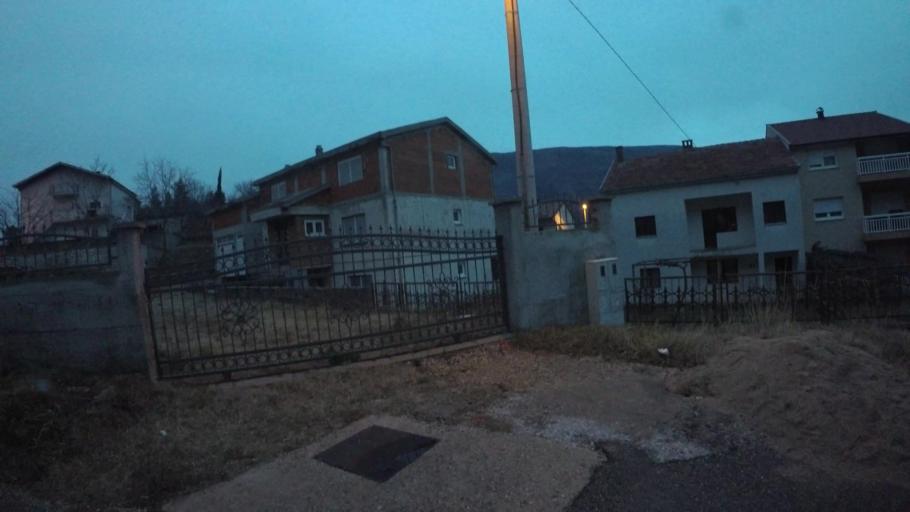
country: BA
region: Federation of Bosnia and Herzegovina
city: Rodoc
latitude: 43.3248
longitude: 17.8179
